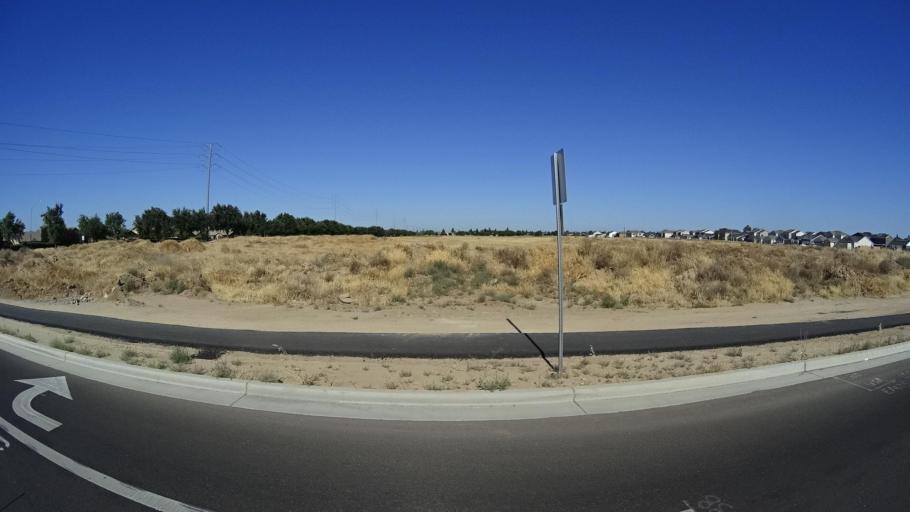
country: US
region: California
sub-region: Fresno County
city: Sunnyside
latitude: 36.7155
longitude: -119.6820
